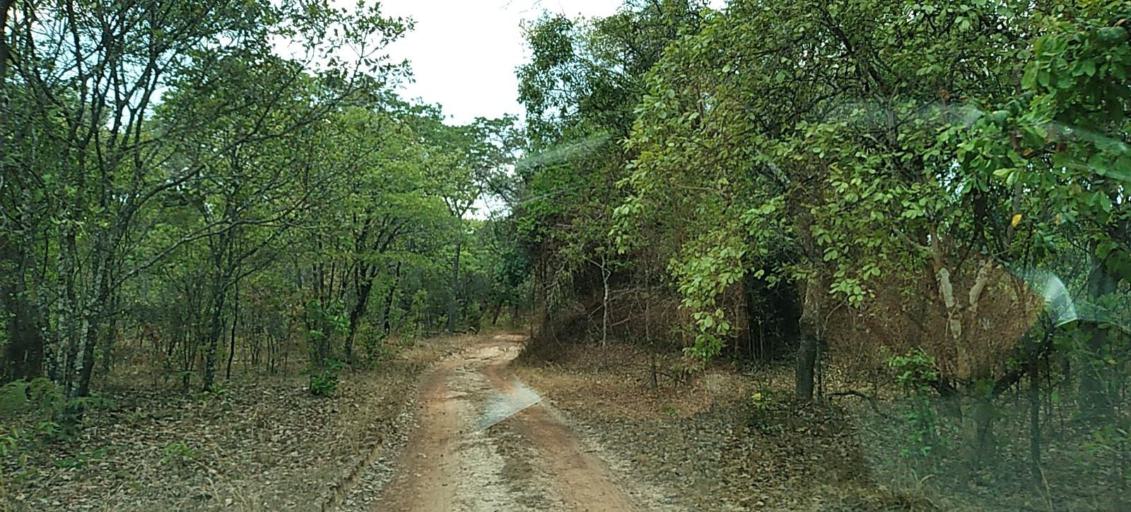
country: ZM
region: Copperbelt
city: Chililabombwe
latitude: -12.4752
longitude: 27.7006
